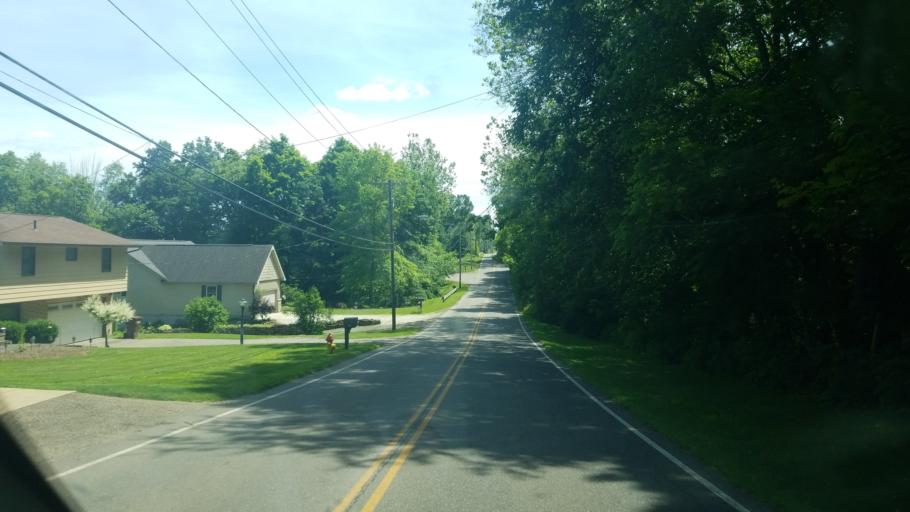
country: US
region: Ohio
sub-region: Stark County
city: Massillon
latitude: 40.8039
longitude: -81.5435
